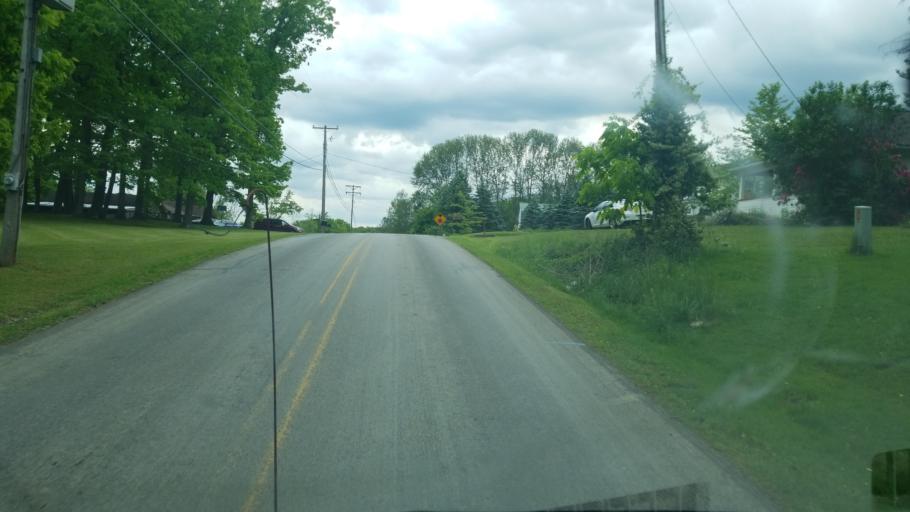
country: US
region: Pennsylvania
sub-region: Venango County
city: Franklin
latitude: 41.2022
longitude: -79.8443
